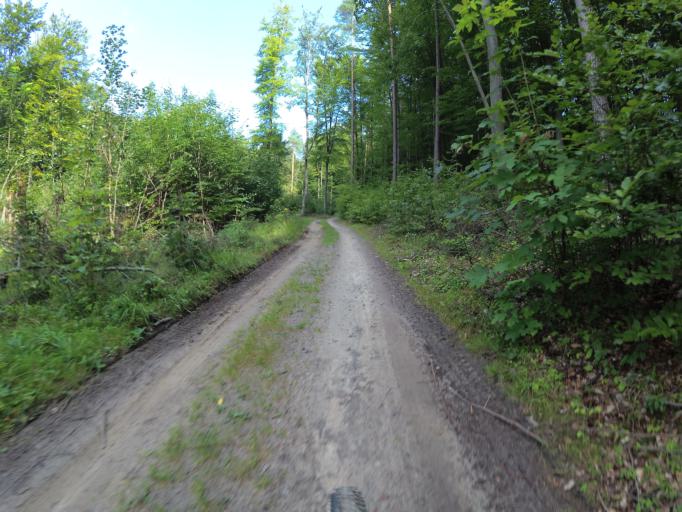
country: PL
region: Pomeranian Voivodeship
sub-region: Gdynia
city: Wielki Kack
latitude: 54.4929
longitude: 18.4755
